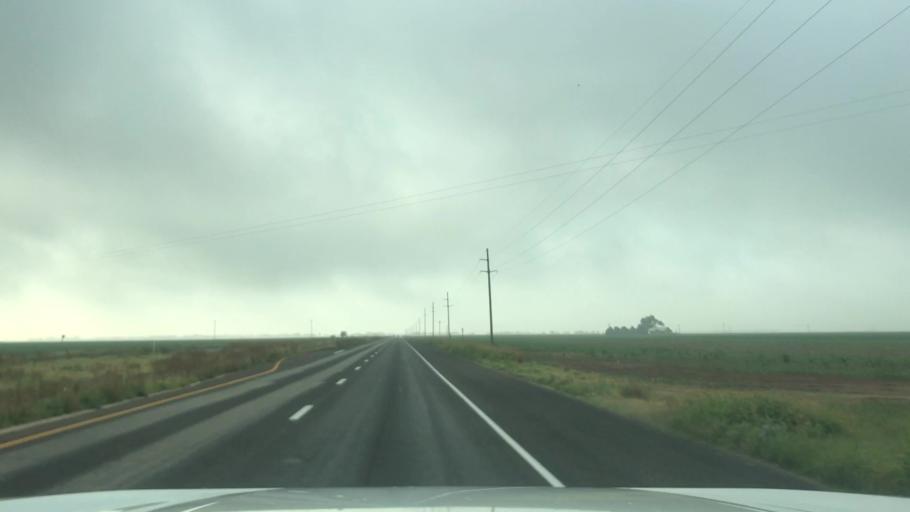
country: US
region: Texas
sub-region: Lubbock County
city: Slaton
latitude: 33.3747
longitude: -101.5774
